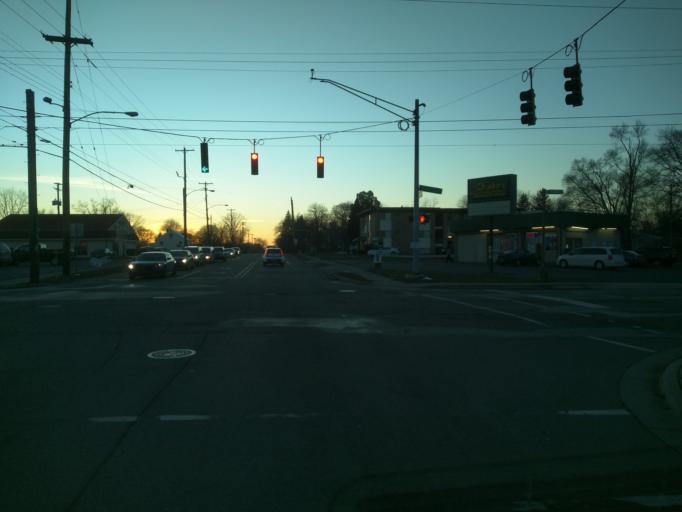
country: US
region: Michigan
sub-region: Ingham County
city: Lansing
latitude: 42.6976
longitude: -84.5821
